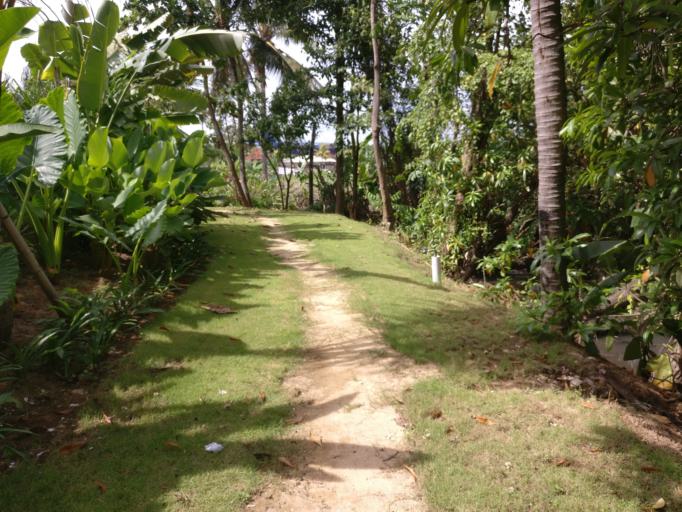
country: ID
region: Bali
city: Banjar Pasekan
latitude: -8.5967
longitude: 115.3384
